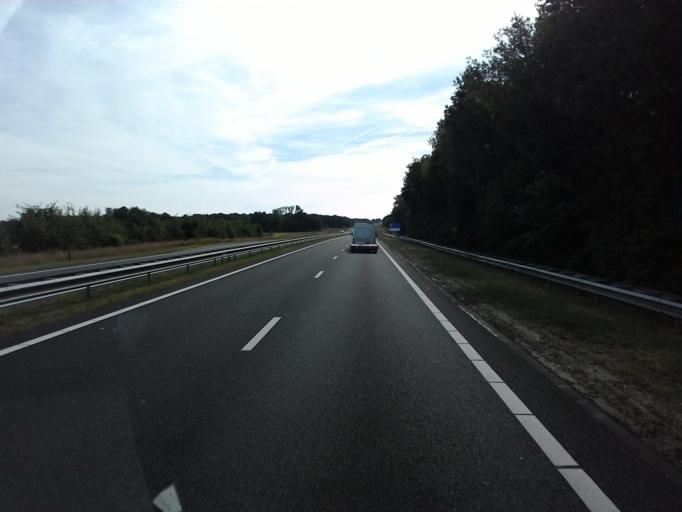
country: NL
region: Drenthe
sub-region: Gemeente Assen
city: Assen
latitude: 52.9686
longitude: 6.5871
